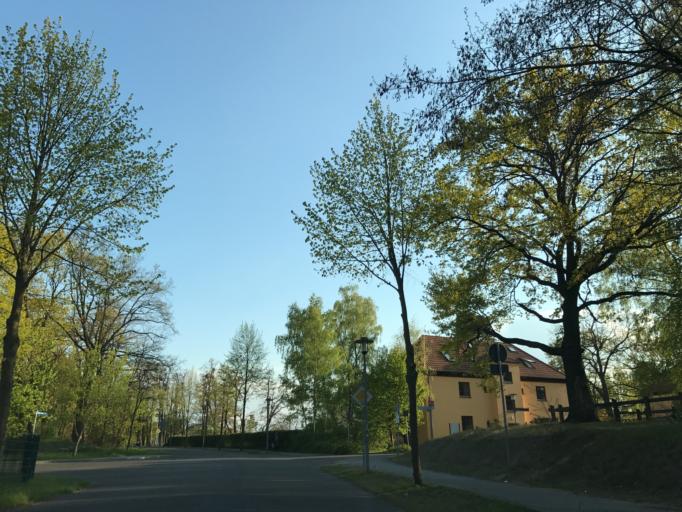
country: DE
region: Brandenburg
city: Brieselang
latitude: 52.5430
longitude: 13.0051
